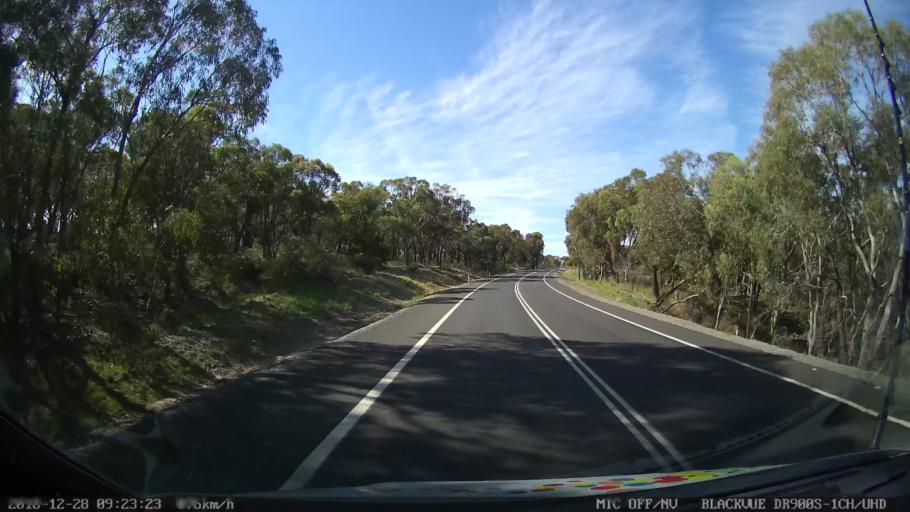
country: AU
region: New South Wales
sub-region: Upper Lachlan Shire
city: Crookwell
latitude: -34.3848
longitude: 149.3843
